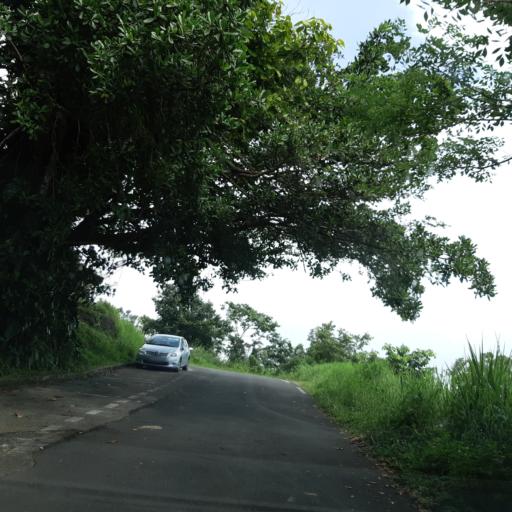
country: GP
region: Guadeloupe
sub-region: Guadeloupe
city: Saint-Claude
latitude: 16.0315
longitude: -61.6810
